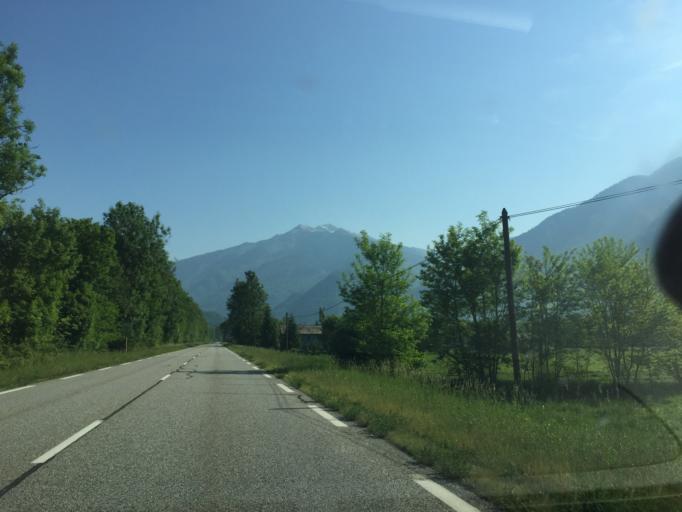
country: FR
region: Rhone-Alpes
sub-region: Departement de la Savoie
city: Aiton
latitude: 45.4834
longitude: 6.2936
